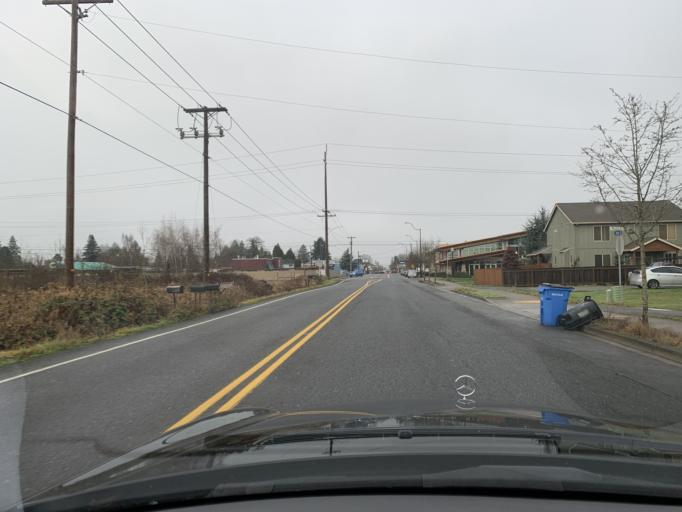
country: US
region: Washington
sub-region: Clark County
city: Battle Ground
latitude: 45.7810
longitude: -122.5258
